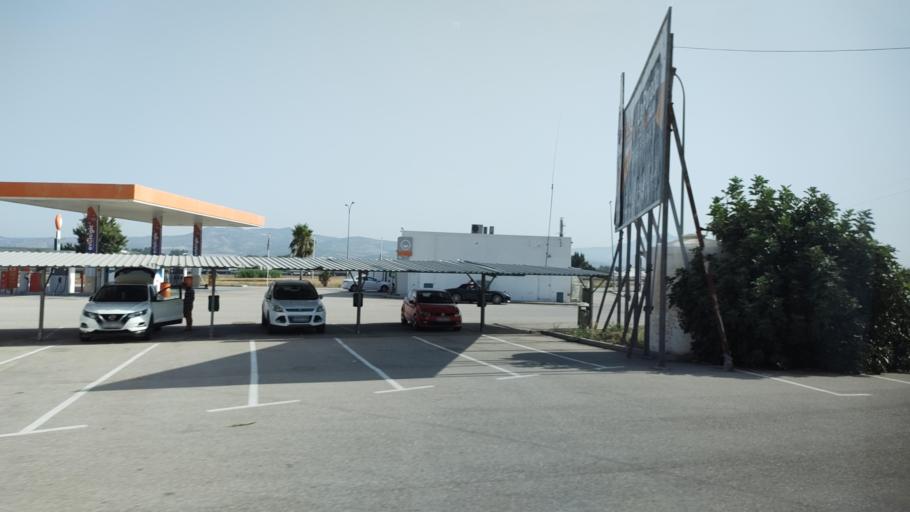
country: ES
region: Andalusia
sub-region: Provincia de Granada
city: Huetor-Tajar
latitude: 37.1793
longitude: -4.0593
